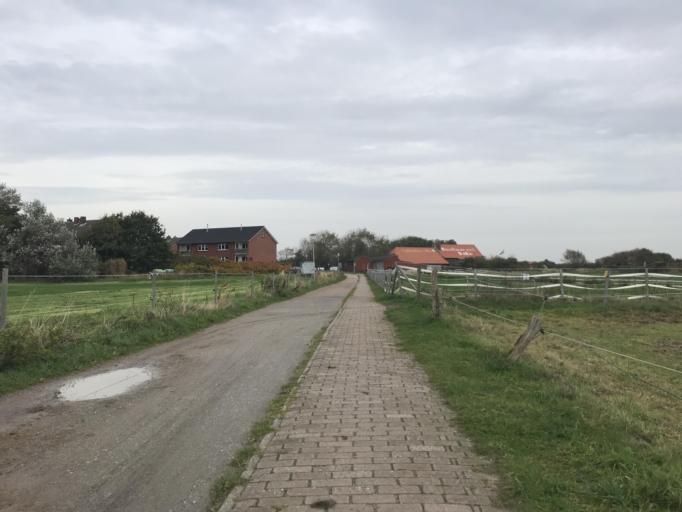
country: DE
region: Lower Saxony
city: Borkum
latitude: 53.5904
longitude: 6.6797
